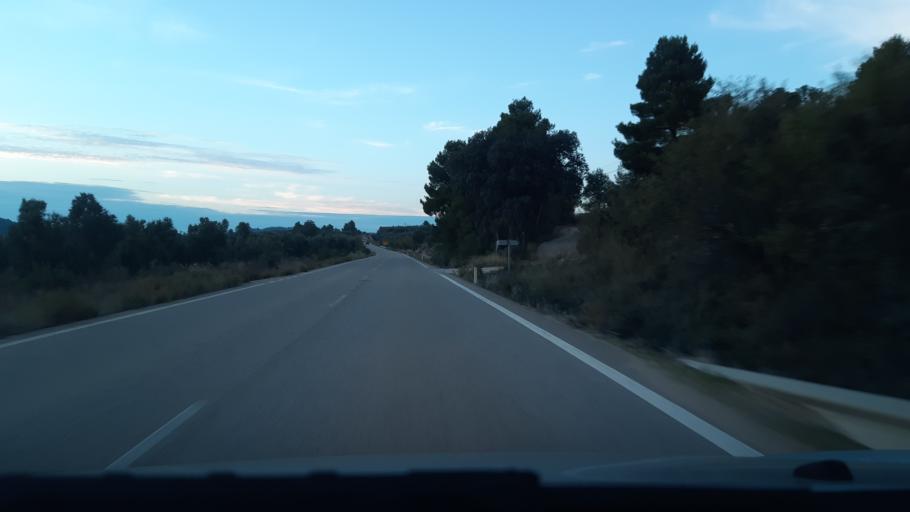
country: ES
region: Aragon
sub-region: Provincia de Teruel
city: Valderrobres
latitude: 40.8555
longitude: 0.1721
